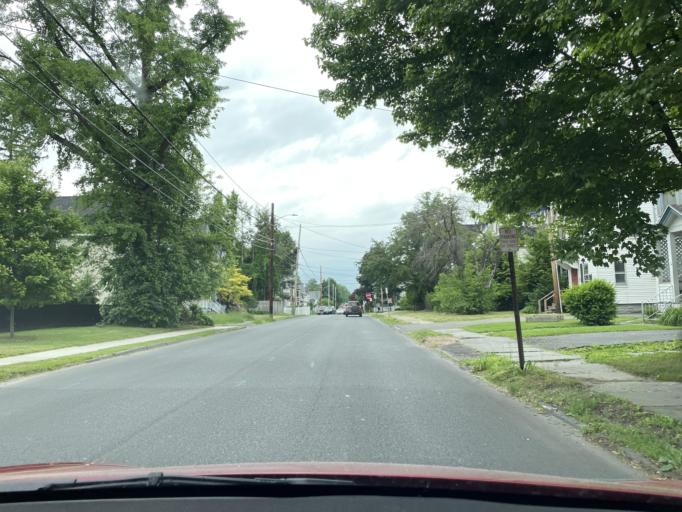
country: US
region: New York
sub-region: Ulster County
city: Kingston
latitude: 41.9305
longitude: -74.0215
